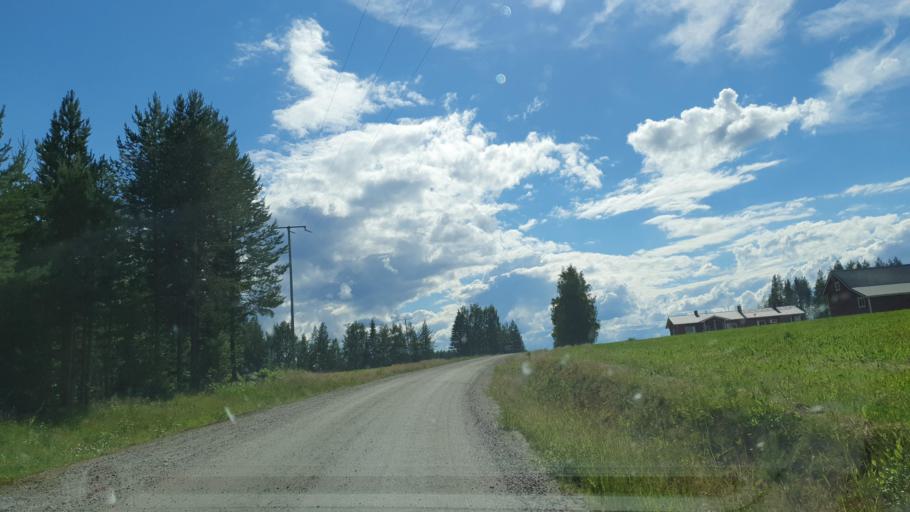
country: FI
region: Kainuu
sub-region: Kehys-Kainuu
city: Kuhmo
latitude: 64.1491
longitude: 29.7879
